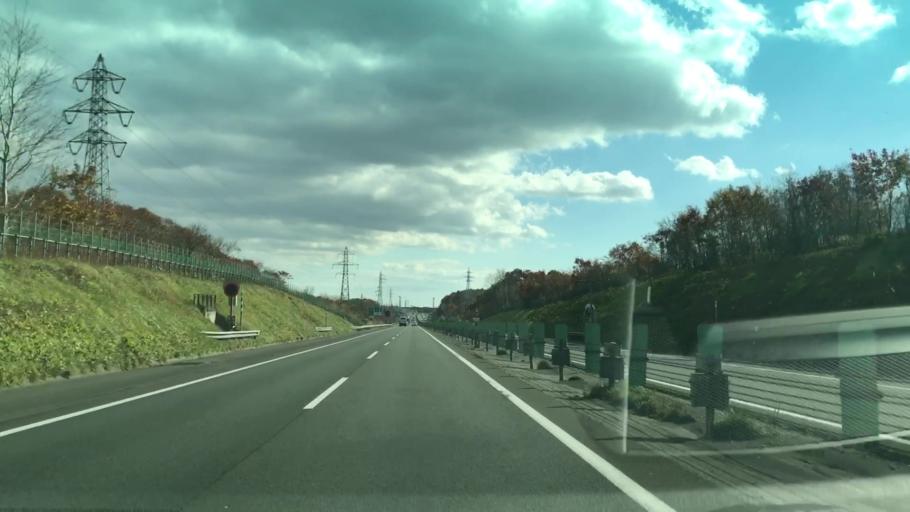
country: JP
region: Hokkaido
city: Kitahiroshima
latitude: 42.9610
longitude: 141.5000
